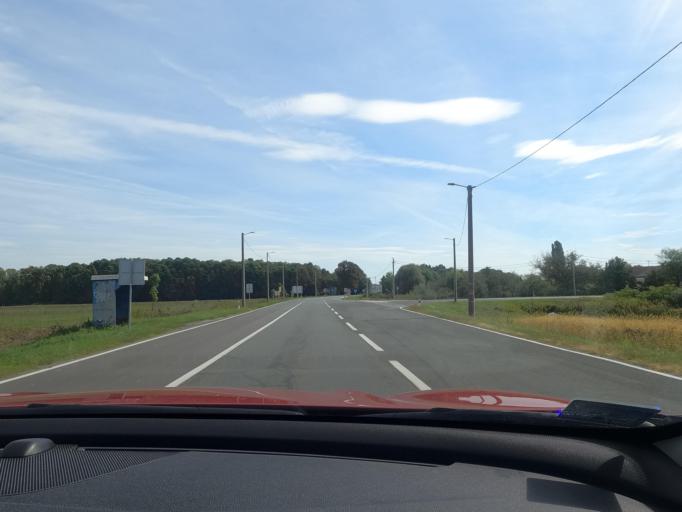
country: HR
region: Sisacko-Moslavacka
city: Budasevo
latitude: 45.4862
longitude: 16.4663
